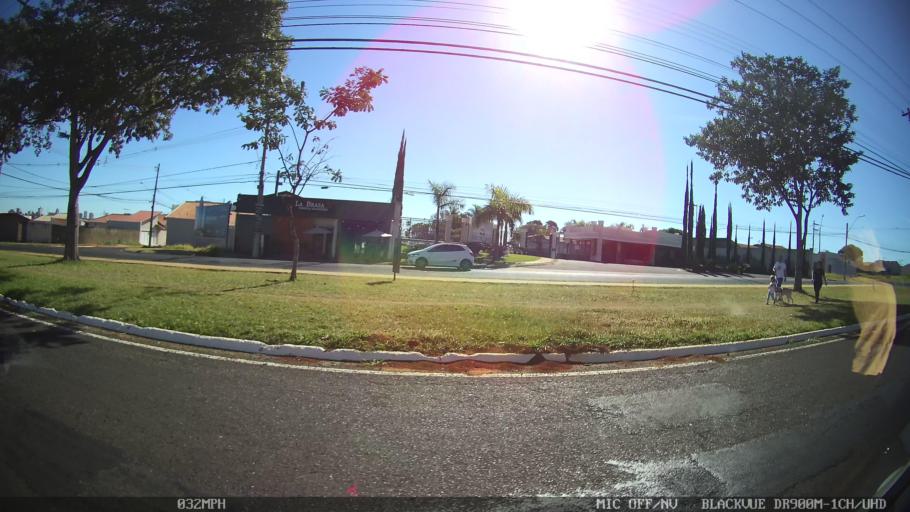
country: BR
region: Sao Paulo
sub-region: Franca
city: Franca
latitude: -20.5580
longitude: -47.3808
